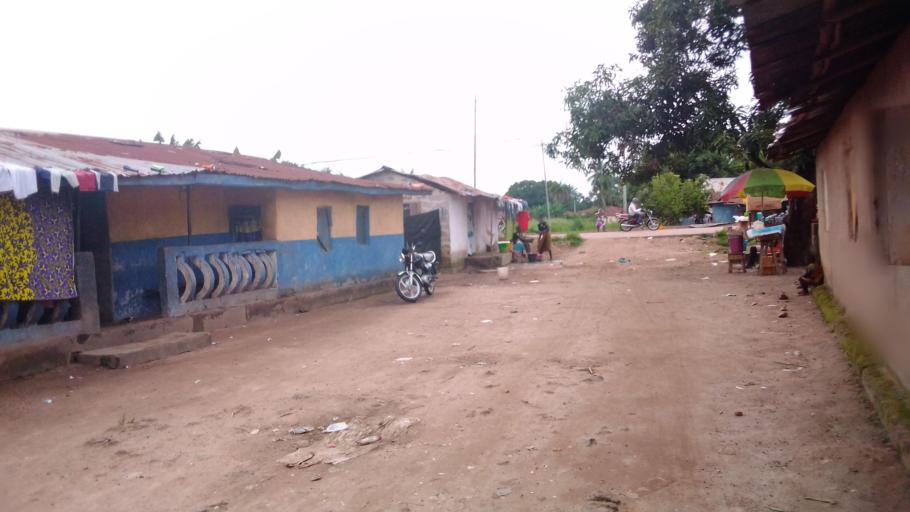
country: SL
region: Northern Province
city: Makeni
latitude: 8.8777
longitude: -12.0431
